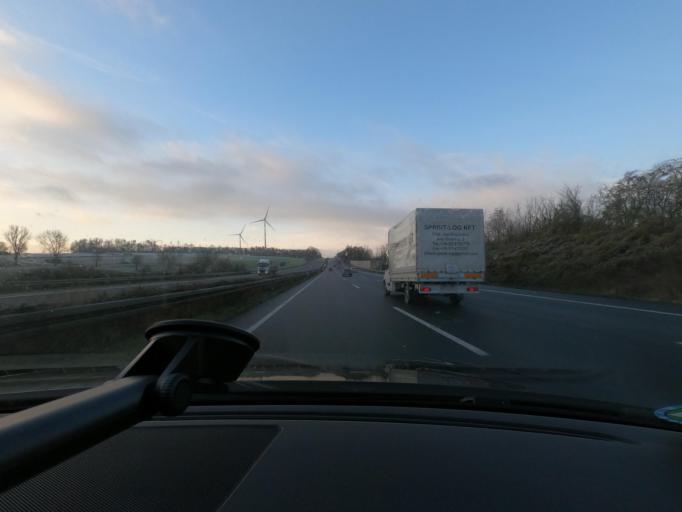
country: DE
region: Hesse
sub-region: Regierungsbezirk Kassel
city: Fuldatal
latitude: 51.3441
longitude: 9.5993
